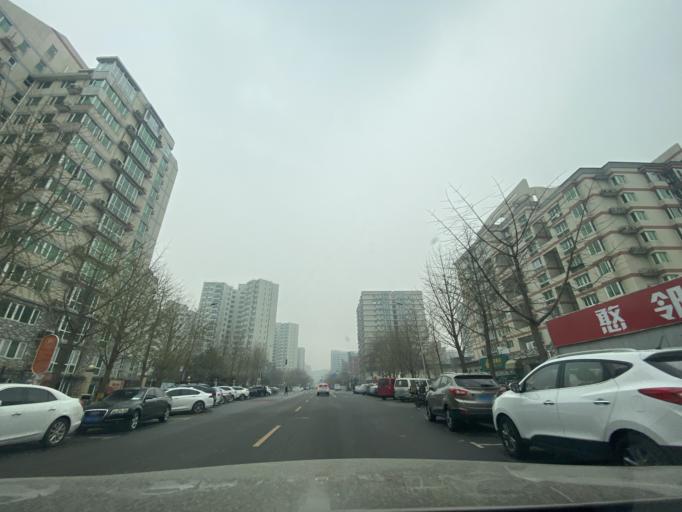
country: CN
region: Beijing
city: Sijiqing
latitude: 39.9611
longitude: 116.2741
